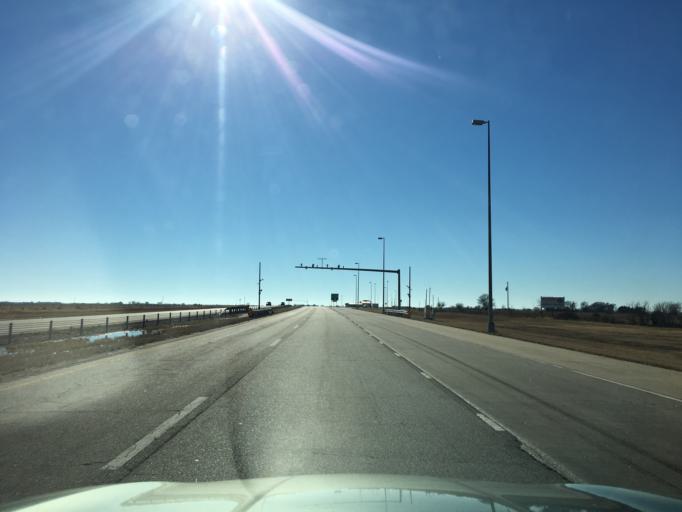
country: US
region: Oklahoma
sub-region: Kay County
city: Blackwell
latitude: 36.9913
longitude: -97.3449
